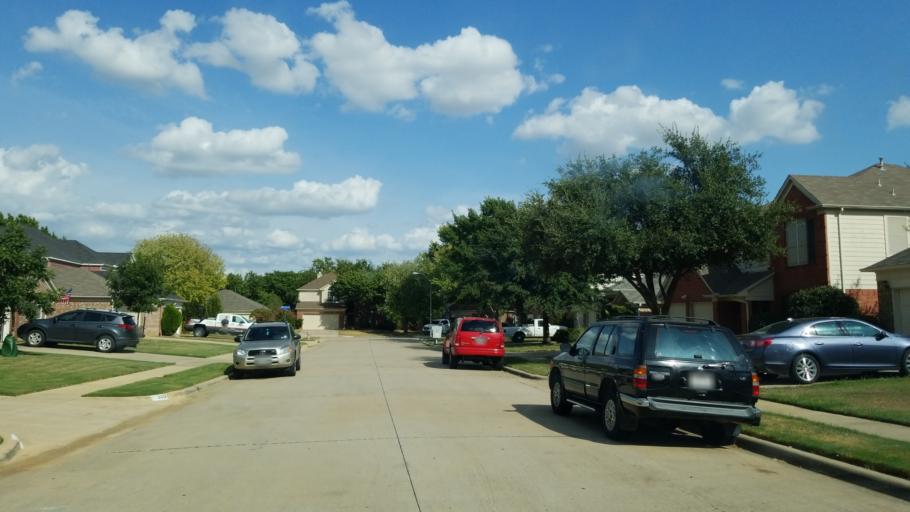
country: US
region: Texas
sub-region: Tarrant County
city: Euless
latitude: 32.8496
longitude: -97.0780
